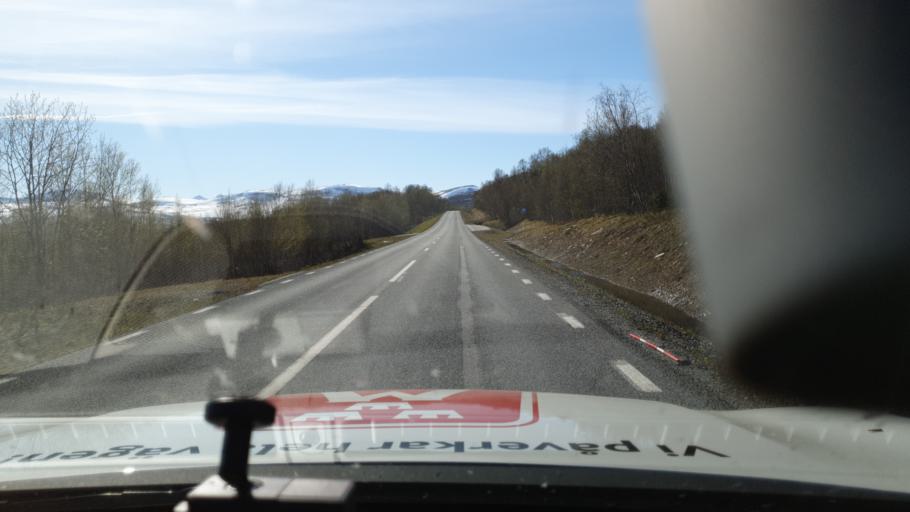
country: NO
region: Nordland
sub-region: Rana
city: Mo i Rana
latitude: 66.0478
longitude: 14.9621
